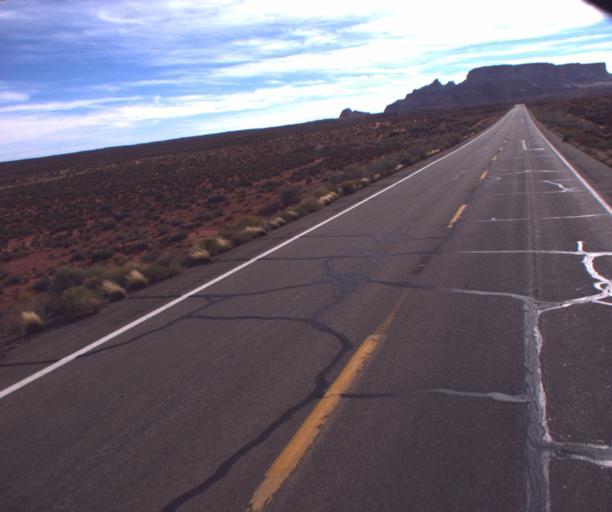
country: US
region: Arizona
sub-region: Coconino County
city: LeChee
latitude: 36.8837
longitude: -111.3551
